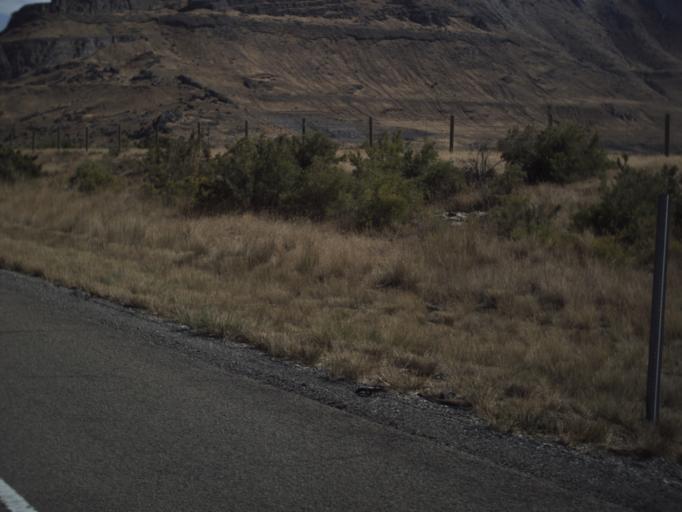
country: US
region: Utah
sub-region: Tooele County
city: Grantsville
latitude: 40.7462
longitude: -112.6591
